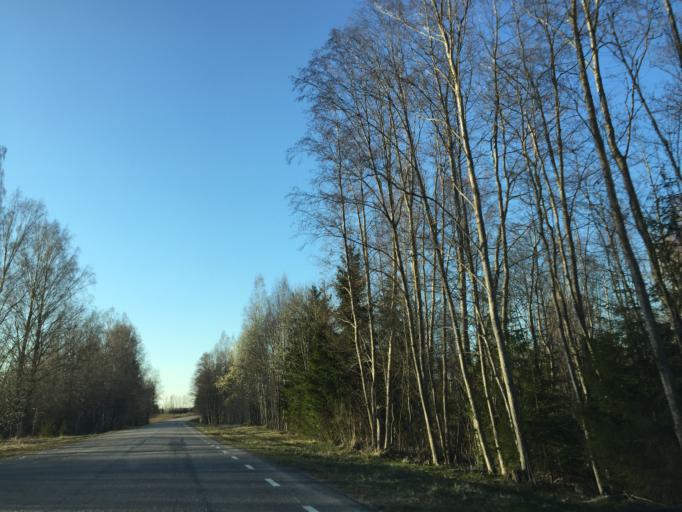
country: EE
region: Ida-Virumaa
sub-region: Toila vald
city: Voka
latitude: 59.1792
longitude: 27.5654
